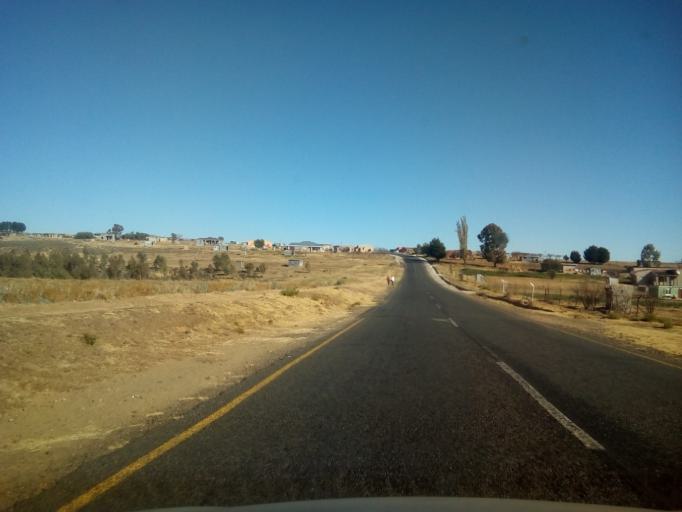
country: LS
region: Maseru
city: Maseru
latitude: -29.2930
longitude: 27.6227
